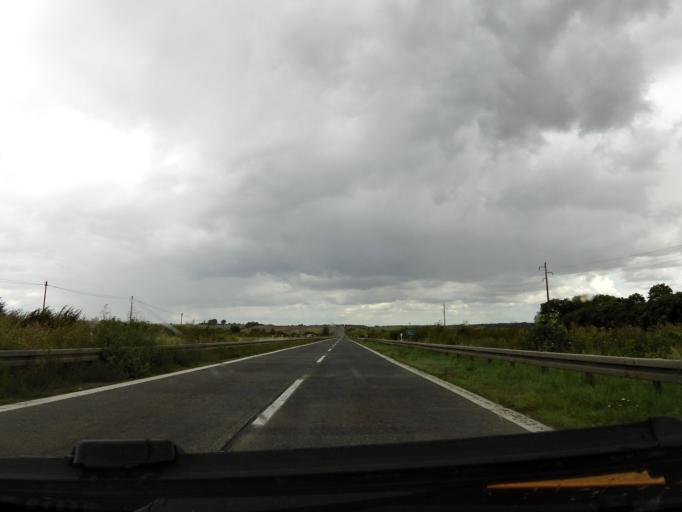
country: DE
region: Brandenburg
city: Gramzow
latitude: 53.2799
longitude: 14.0708
